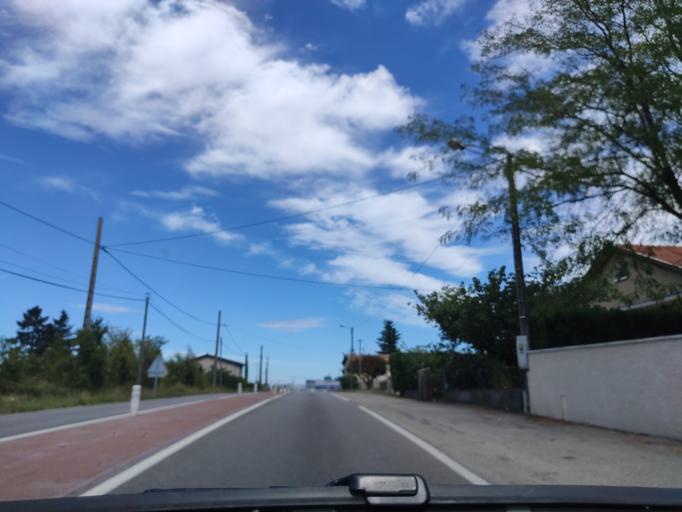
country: FR
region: Rhone-Alpes
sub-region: Departement de l'Isere
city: Roussillon
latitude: 45.3895
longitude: 4.8041
